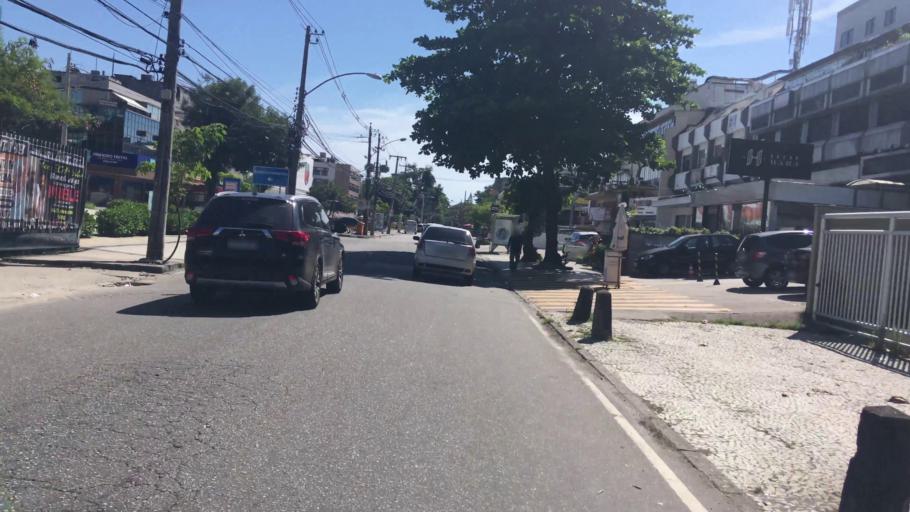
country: BR
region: Rio de Janeiro
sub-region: Rio De Janeiro
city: Rio de Janeiro
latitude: -23.0082
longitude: -43.3051
